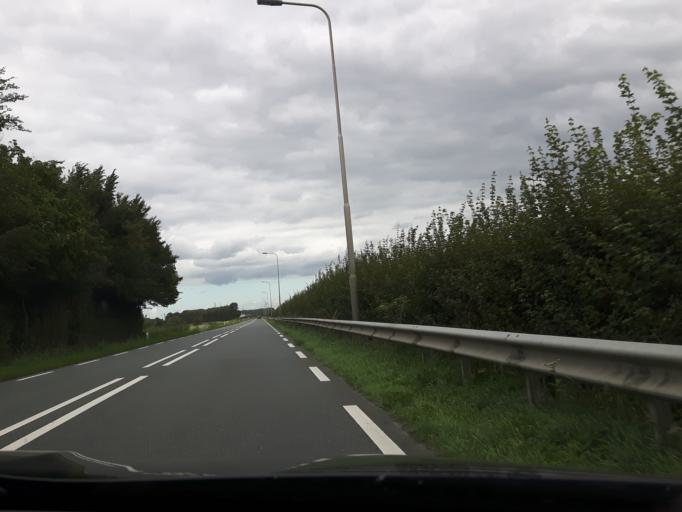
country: NL
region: Zeeland
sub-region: Gemeente Terneuzen
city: Westdorpe
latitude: 51.2485
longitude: 3.8187
